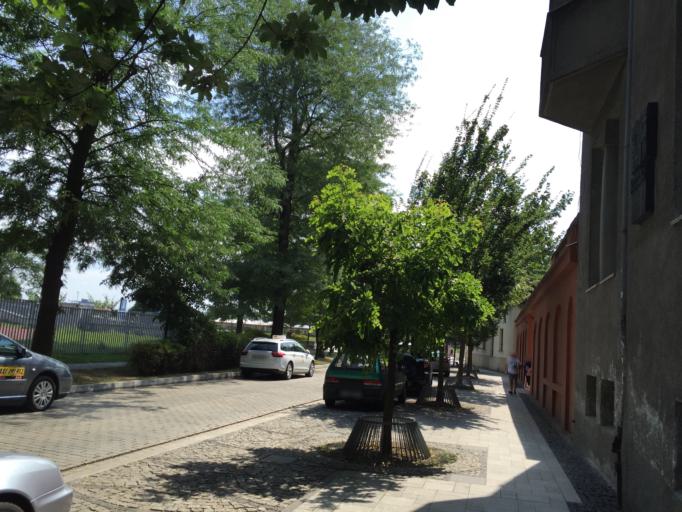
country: PL
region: Lesser Poland Voivodeship
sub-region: Krakow
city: Krakow
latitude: 50.0561
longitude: 19.9320
